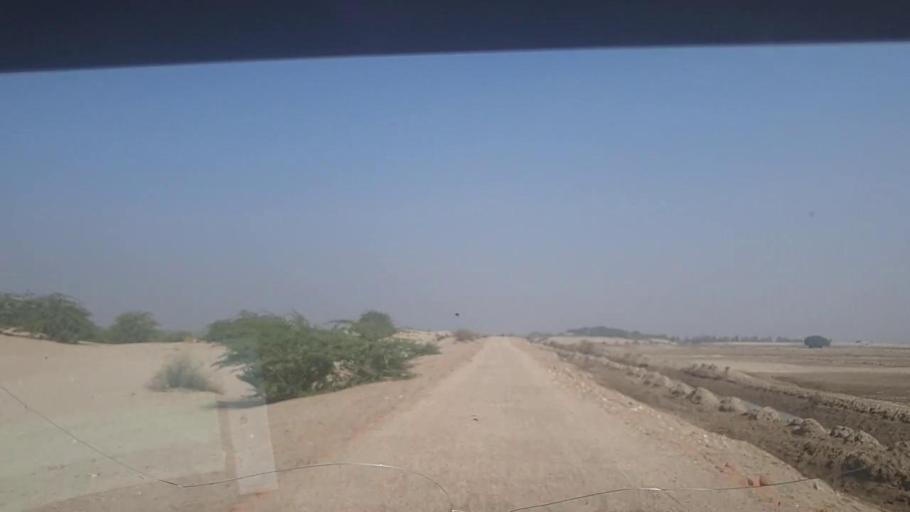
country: PK
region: Sindh
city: Khairpur
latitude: 27.4488
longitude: 68.7197
